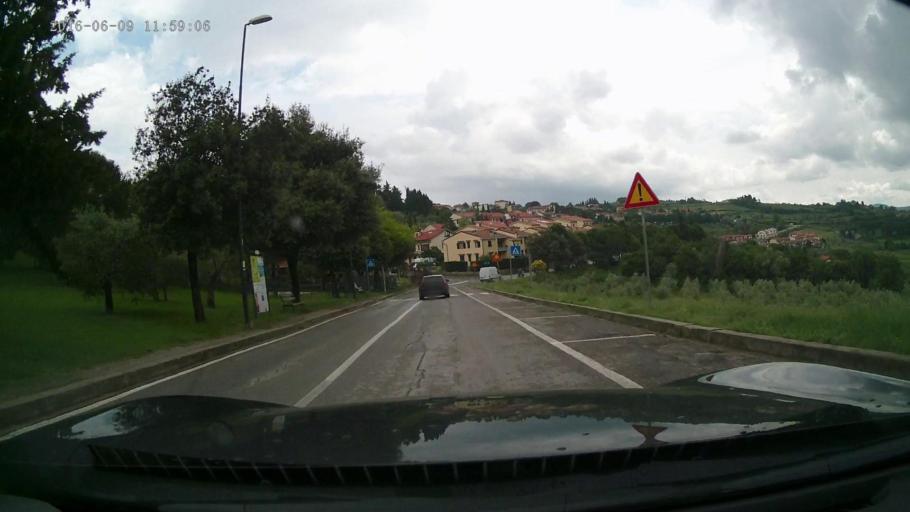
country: IT
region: Tuscany
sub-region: Province of Florence
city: Panzano in Chianti
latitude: 43.5452
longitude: 11.3106
